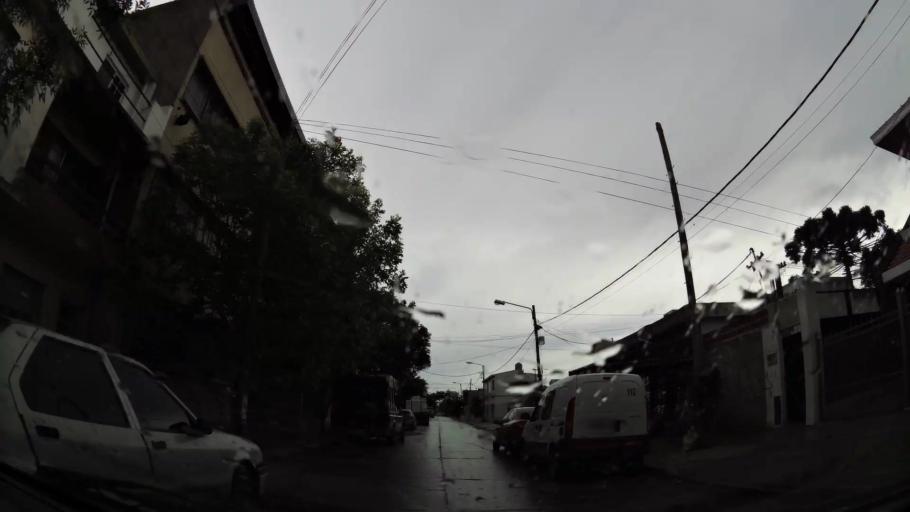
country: AR
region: Buenos Aires
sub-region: Partido de Quilmes
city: Quilmes
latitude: -34.7725
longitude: -58.2226
